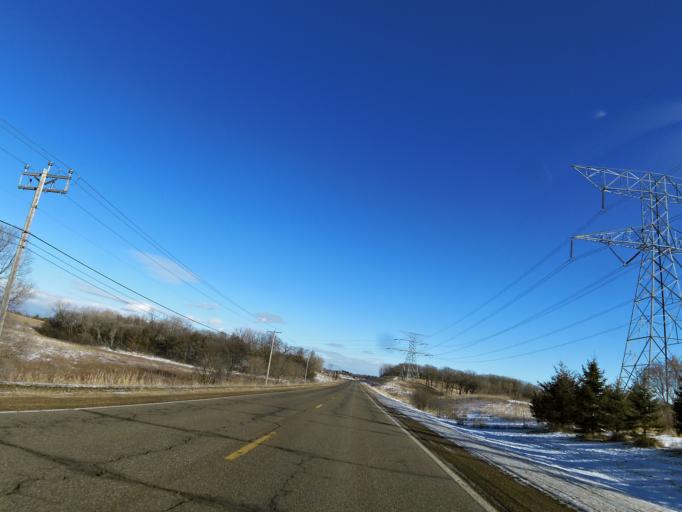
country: US
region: Minnesota
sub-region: Washington County
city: Lakeland
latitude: 44.9469
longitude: -92.8261
